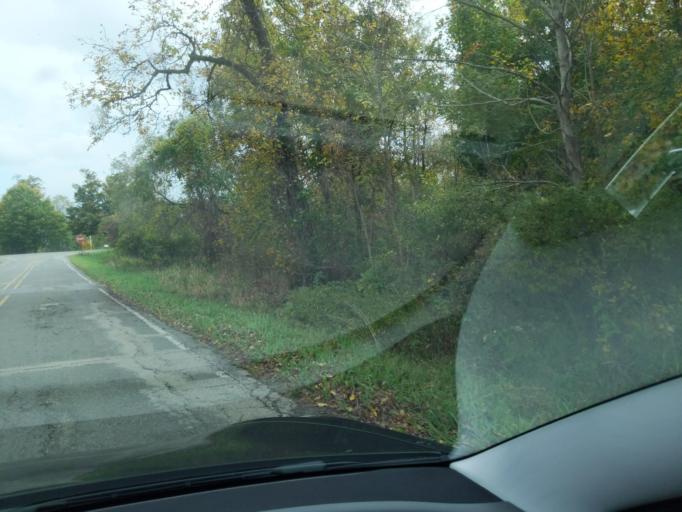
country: US
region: Michigan
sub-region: Ingham County
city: Leslie
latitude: 42.4123
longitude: -84.3539
